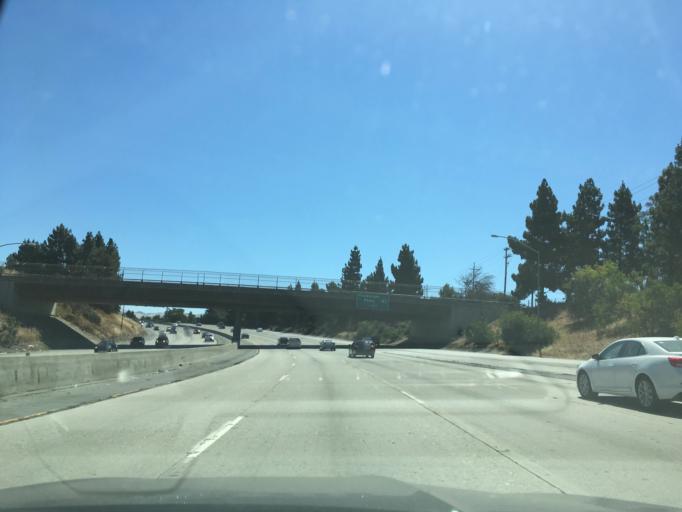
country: US
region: California
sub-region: Santa Clara County
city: Buena Vista
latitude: 37.3146
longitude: -121.9125
